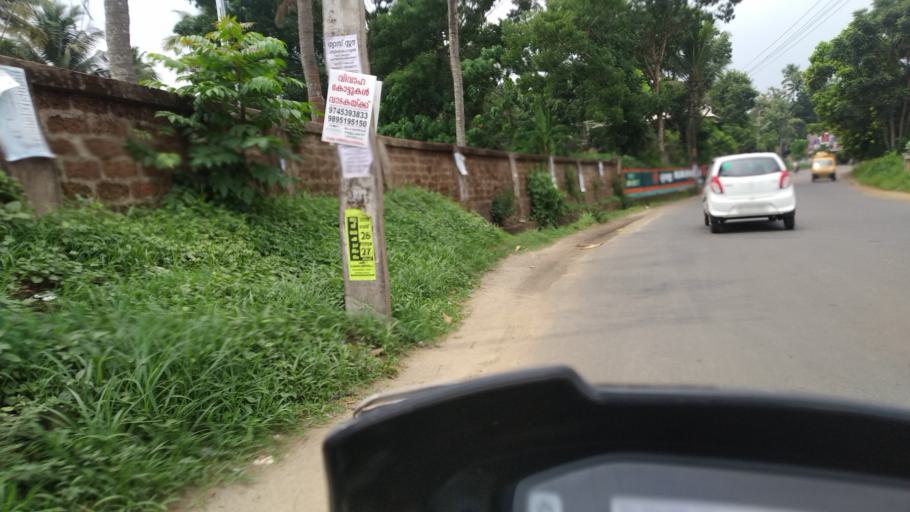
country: IN
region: Kerala
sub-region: Ernakulam
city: Perumpavur
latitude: 10.1124
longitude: 76.5220
